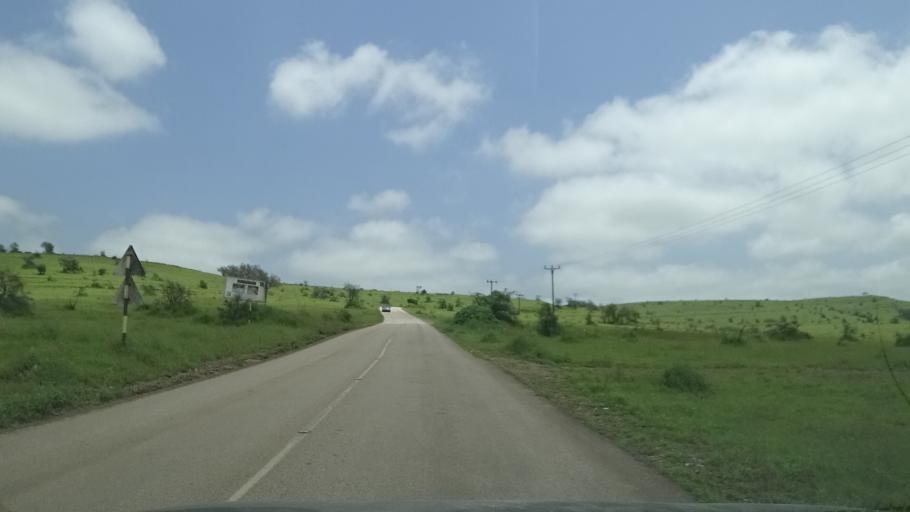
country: OM
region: Zufar
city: Salalah
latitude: 17.2037
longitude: 54.1862
